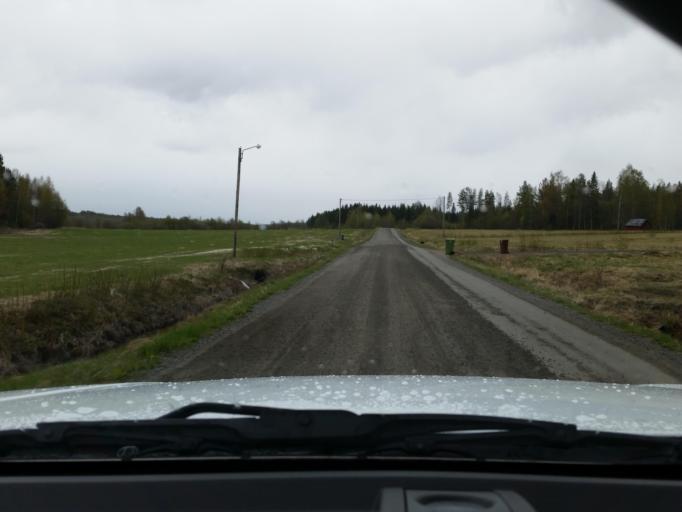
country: SE
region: Norrbotten
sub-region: Pitea Kommun
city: Norrfjarden
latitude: 65.5474
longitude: 21.4885
